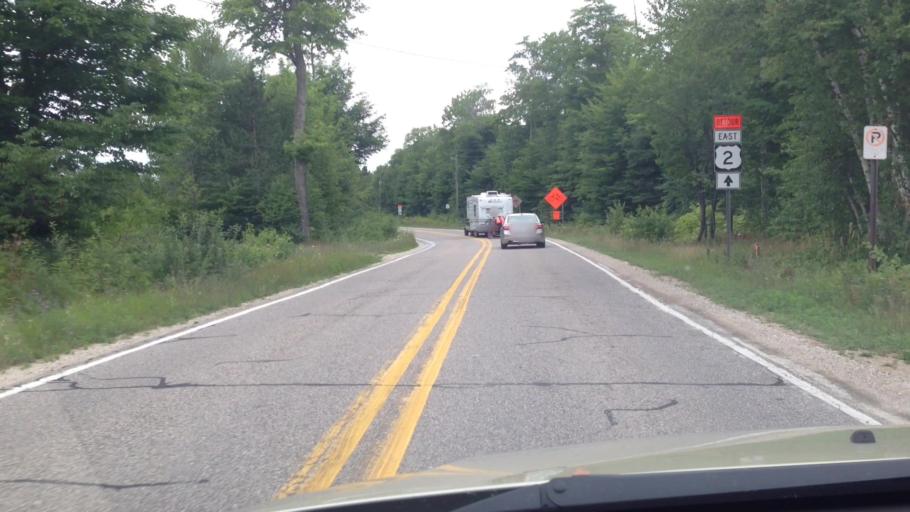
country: US
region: Michigan
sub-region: Mackinac County
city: Saint Ignace
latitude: 46.0539
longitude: -85.1510
